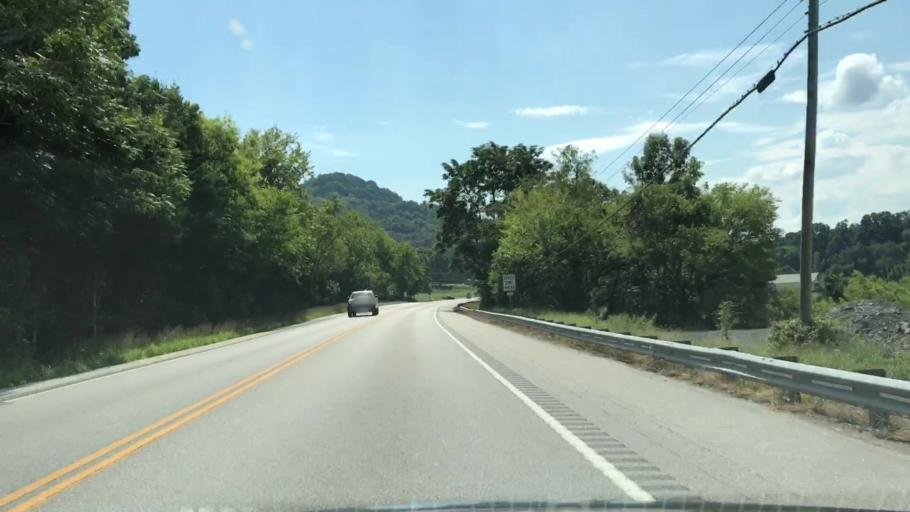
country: US
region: Tennessee
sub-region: Smith County
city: Carthage
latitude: 36.2899
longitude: -85.9939
